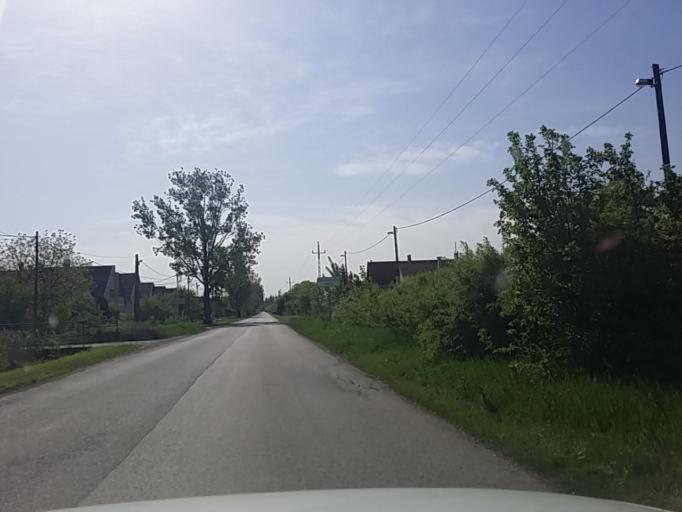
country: HU
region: Bekes
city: Bekes
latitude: 46.7069
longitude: 21.1778
